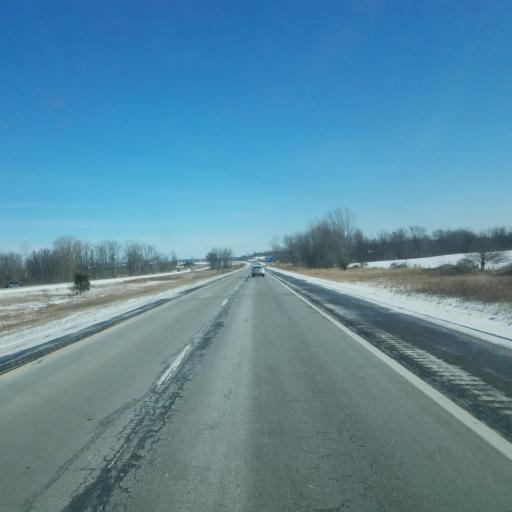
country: US
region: Michigan
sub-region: Livingston County
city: Fowlerville
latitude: 42.6460
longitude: -84.0875
